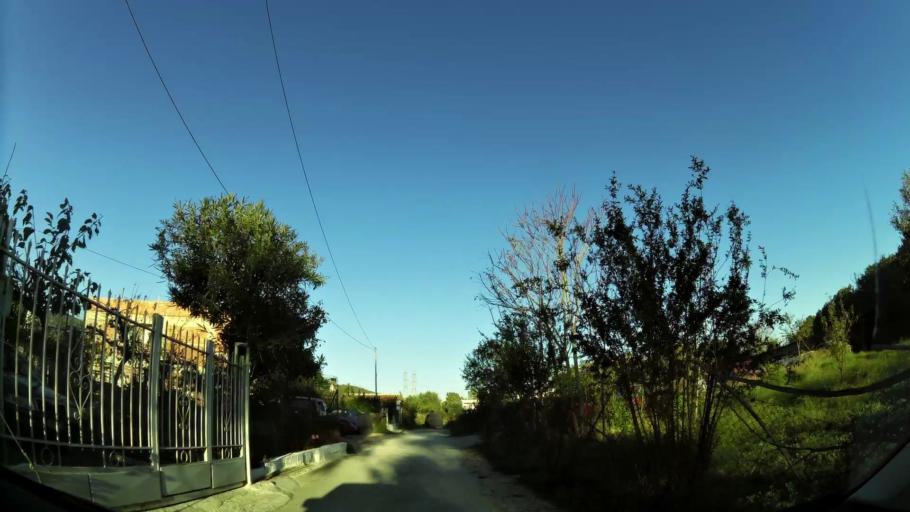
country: GR
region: Attica
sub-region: Nomarchia Anatolikis Attikis
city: Pallini
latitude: 37.9978
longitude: 23.8679
